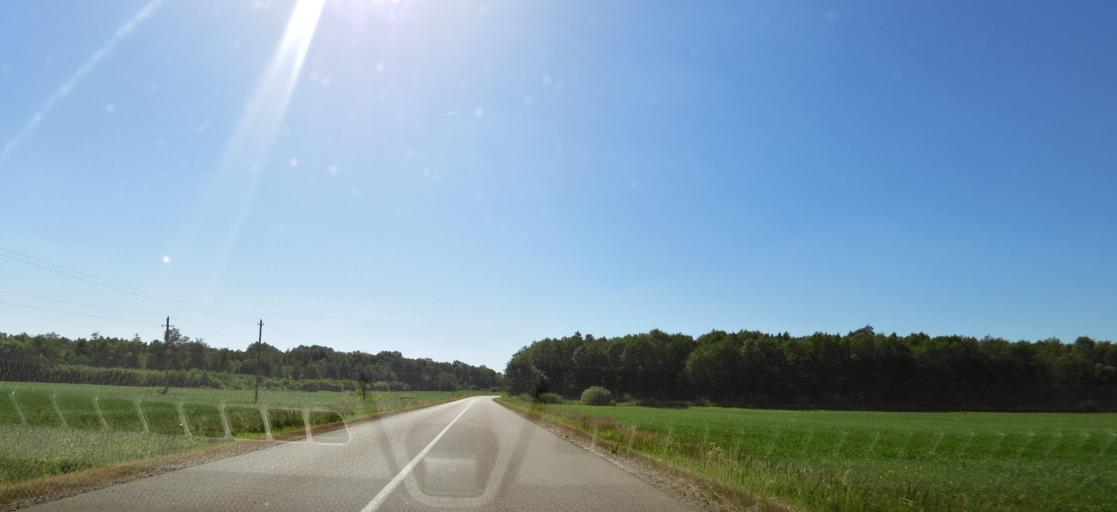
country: LT
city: Vabalninkas
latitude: 56.0027
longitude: 24.6545
